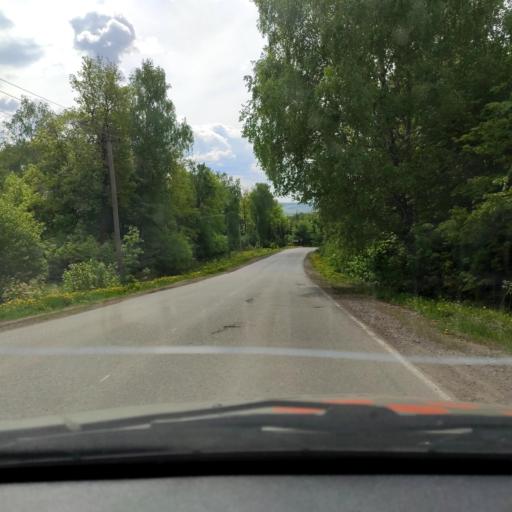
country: RU
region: Bashkortostan
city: Avdon
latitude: 54.6517
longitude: 55.7024
